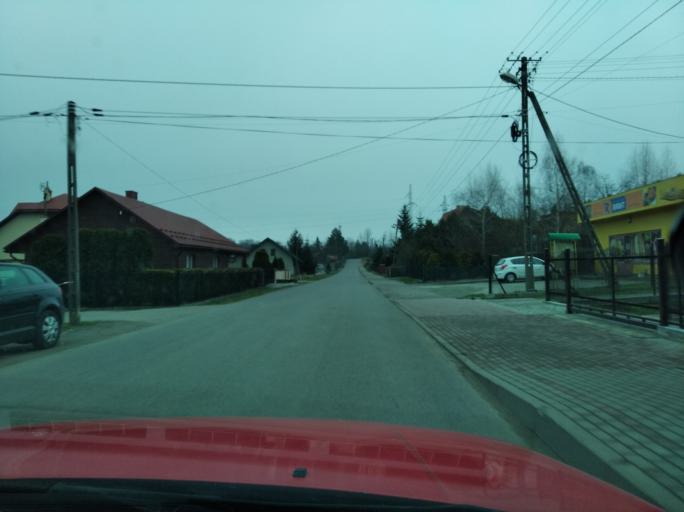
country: PL
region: Subcarpathian Voivodeship
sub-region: Powiat jaroslawski
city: Pawlosiow
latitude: 50.0032
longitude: 22.6532
